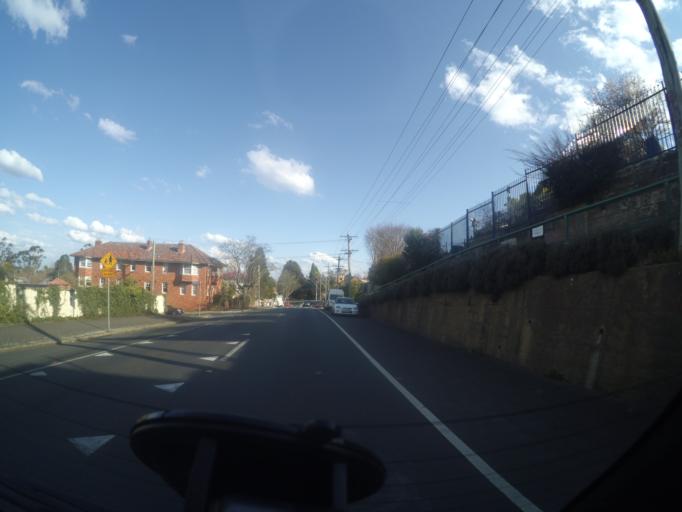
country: AU
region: New South Wales
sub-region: Blue Mountains Municipality
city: Katoomba
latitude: -33.7158
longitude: 150.3125
